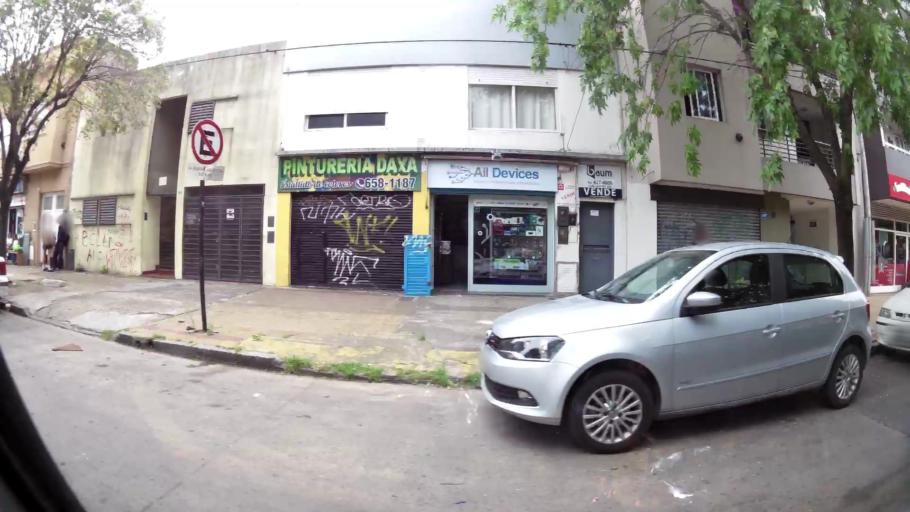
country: AR
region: Buenos Aires
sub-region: Partido de La Plata
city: La Plata
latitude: -34.9403
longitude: -57.9629
